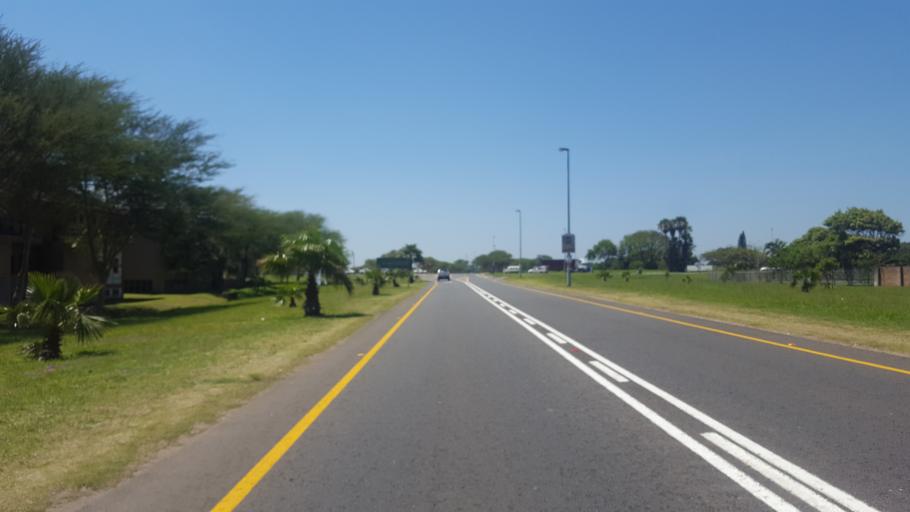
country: ZA
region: KwaZulu-Natal
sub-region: uThungulu District Municipality
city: Richards Bay
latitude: -28.7523
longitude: 32.0547
